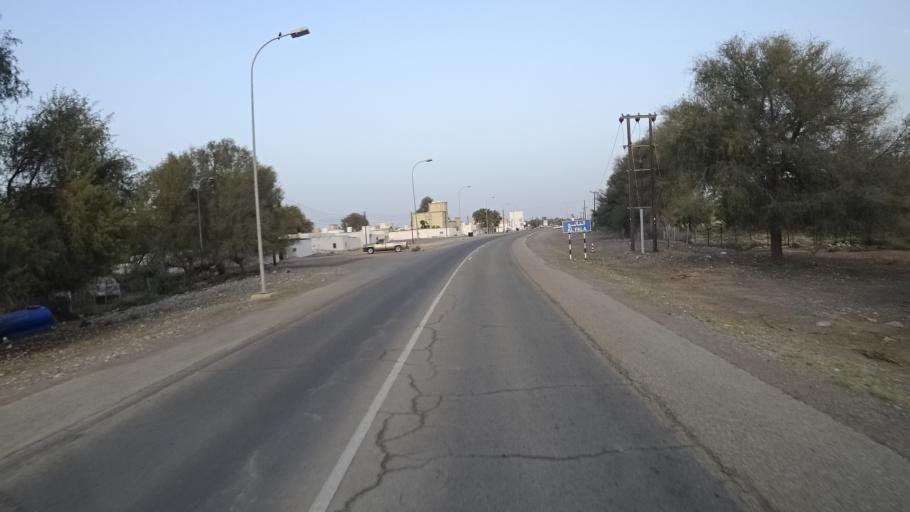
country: OM
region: Muhafazat Masqat
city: Muscat
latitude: 23.2066
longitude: 58.9630
